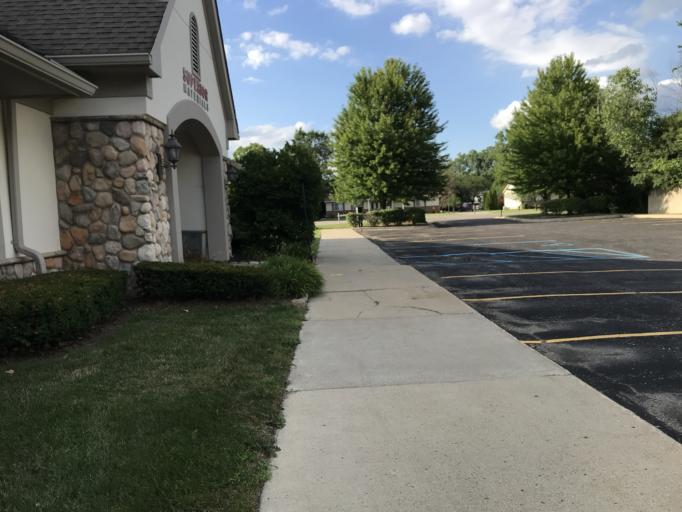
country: US
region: Michigan
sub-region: Oakland County
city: Farmington
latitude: 42.4697
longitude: -83.3513
